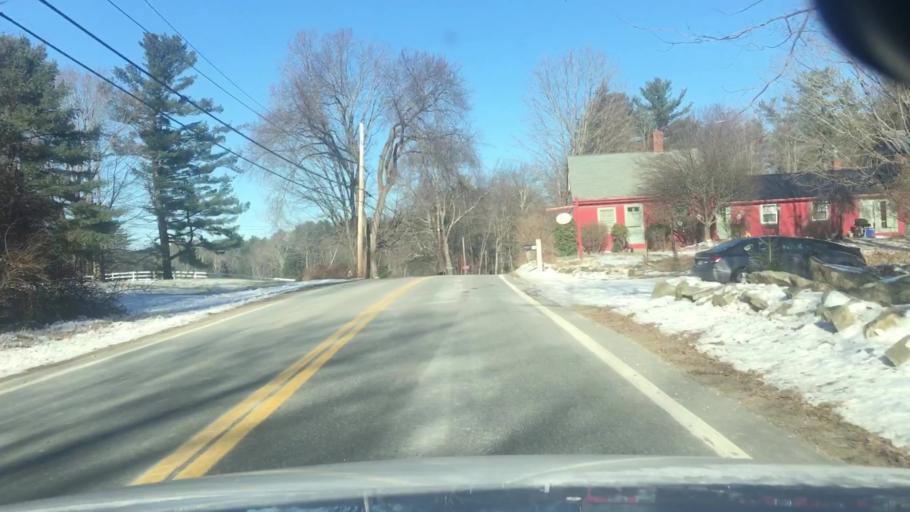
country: US
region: New Hampshire
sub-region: Merrimack County
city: Canterbury
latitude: 43.3079
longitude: -71.5676
